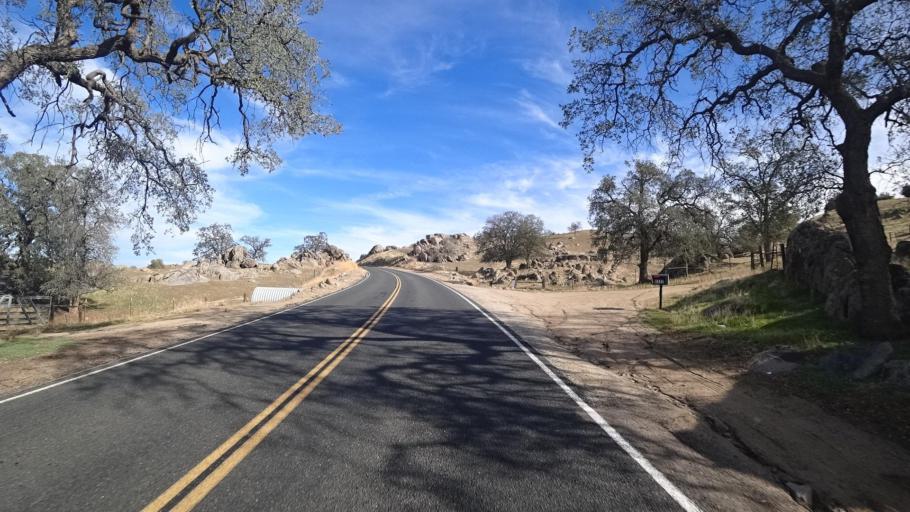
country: US
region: California
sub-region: Kern County
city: Oildale
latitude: 35.6176
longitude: -118.8578
